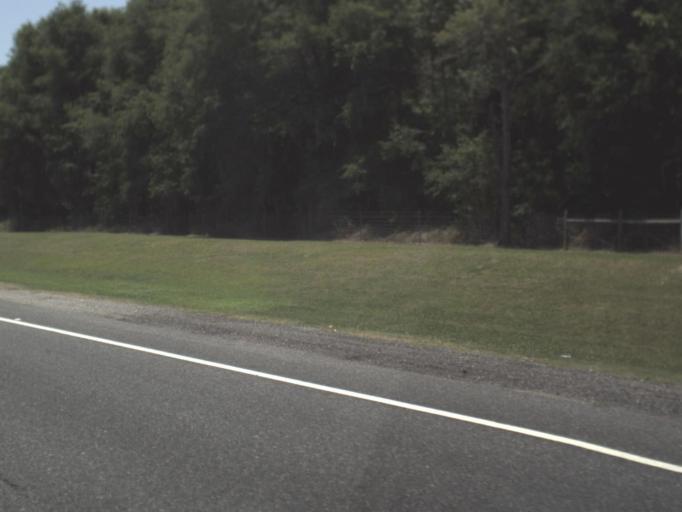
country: US
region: Florida
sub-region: Suwannee County
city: Wellborn
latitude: 30.2732
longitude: -82.7869
